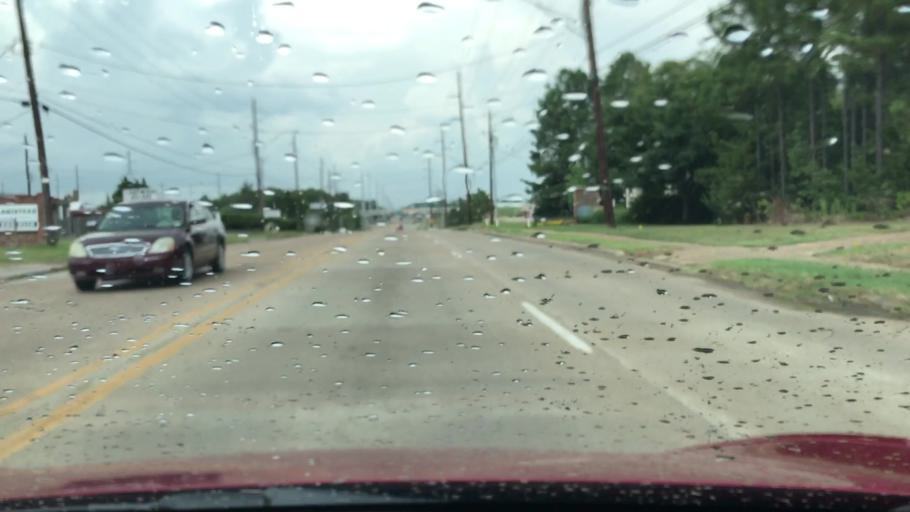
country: US
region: Louisiana
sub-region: Bossier Parish
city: Bossier City
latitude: 32.4191
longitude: -93.7631
